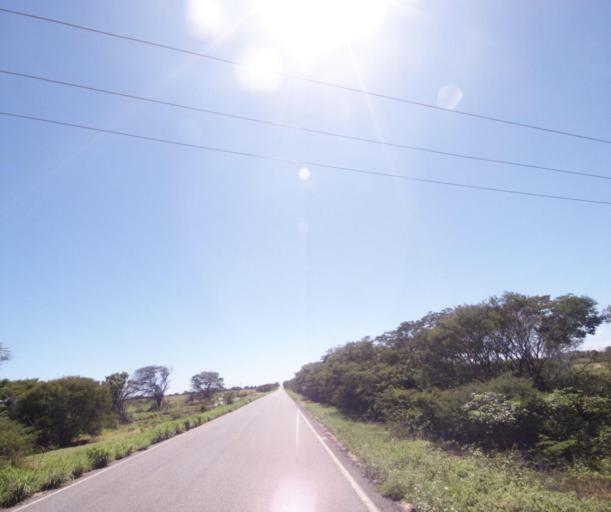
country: BR
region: Bahia
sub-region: Carinhanha
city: Carinhanha
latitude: -14.2846
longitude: -43.5837
